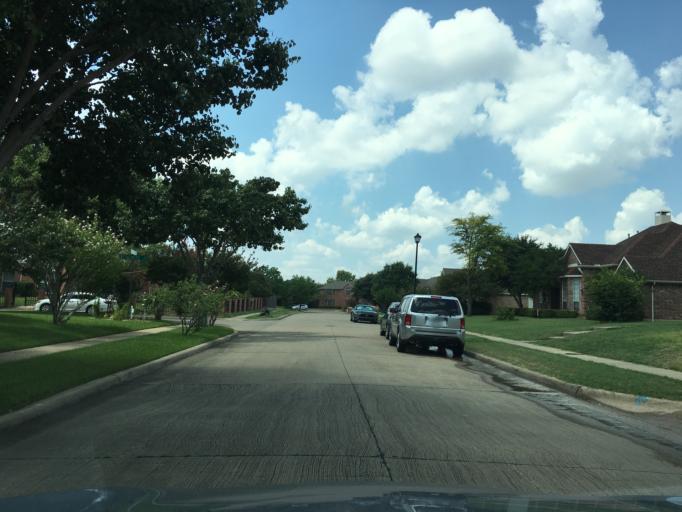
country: US
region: Texas
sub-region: Dallas County
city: Garland
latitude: 32.9430
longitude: -96.6455
